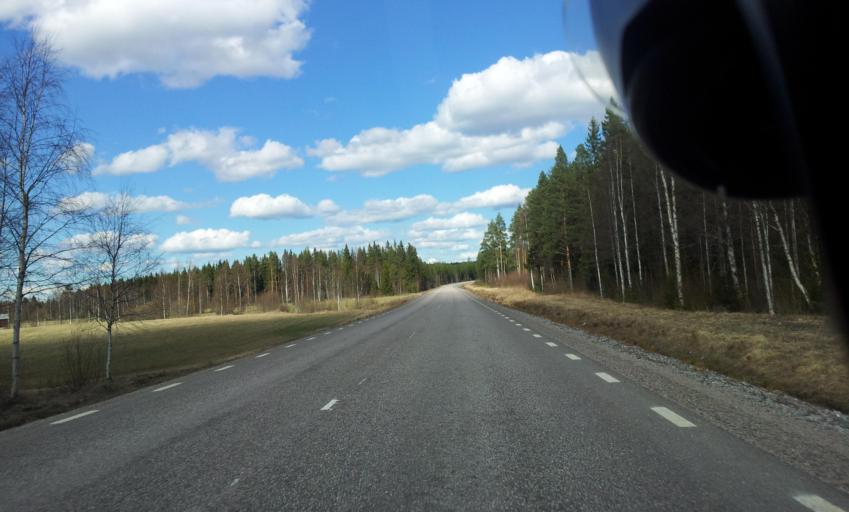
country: SE
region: Gaevleborg
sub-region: Ovanakers Kommun
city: Edsbyn
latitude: 61.2721
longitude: 15.8937
